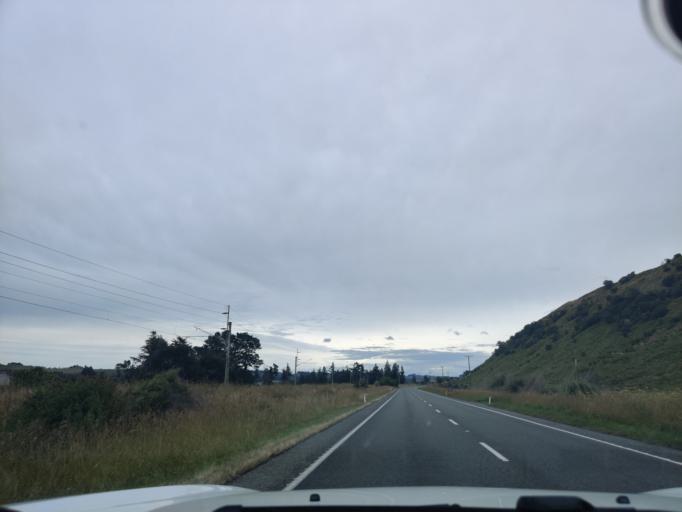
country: NZ
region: Manawatu-Wanganui
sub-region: Ruapehu District
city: Waiouru
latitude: -39.8430
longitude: 175.7410
